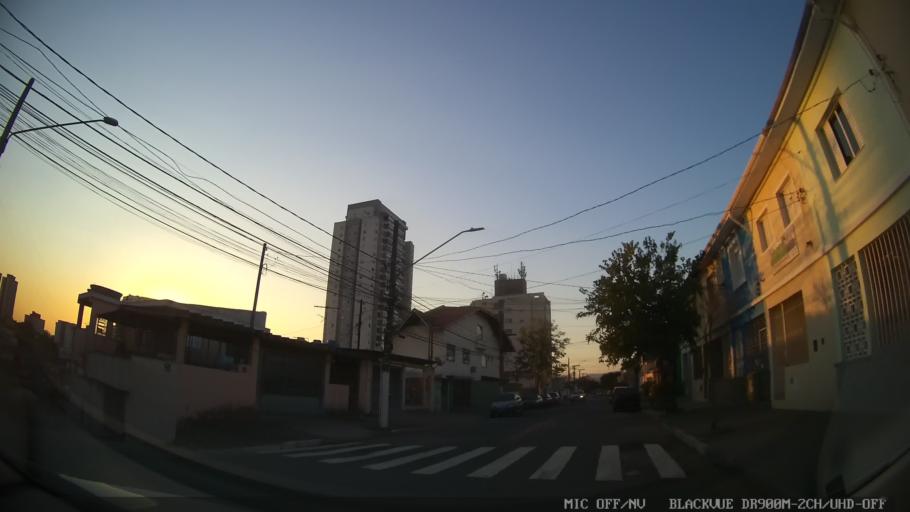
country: BR
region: Sao Paulo
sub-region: Sao Paulo
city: Sao Paulo
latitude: -23.4982
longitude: -46.6433
